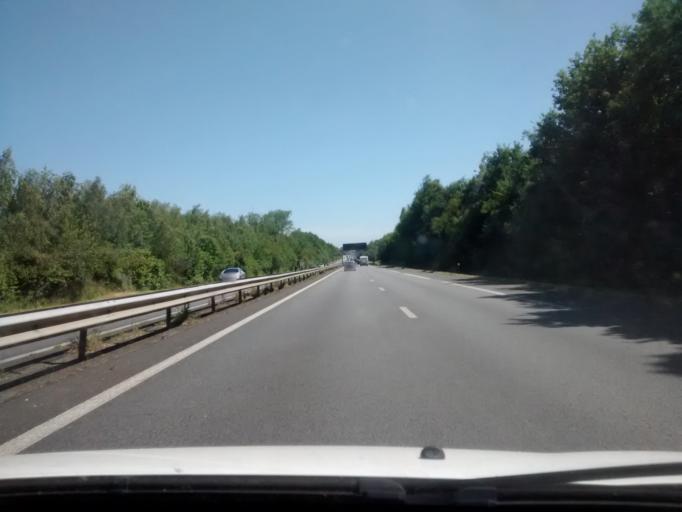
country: FR
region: Brittany
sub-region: Departement d'Ille-et-Vilaine
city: Montgermont
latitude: 48.1680
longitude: -1.7121
